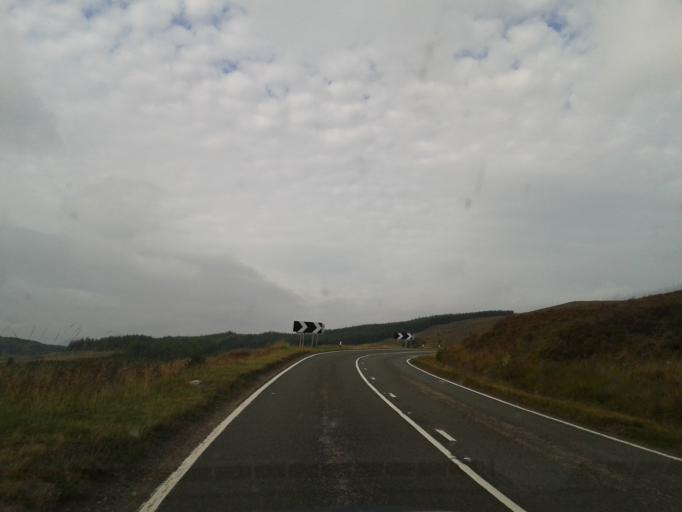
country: GB
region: Scotland
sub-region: Highland
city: Spean Bridge
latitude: 57.0842
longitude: -4.9605
